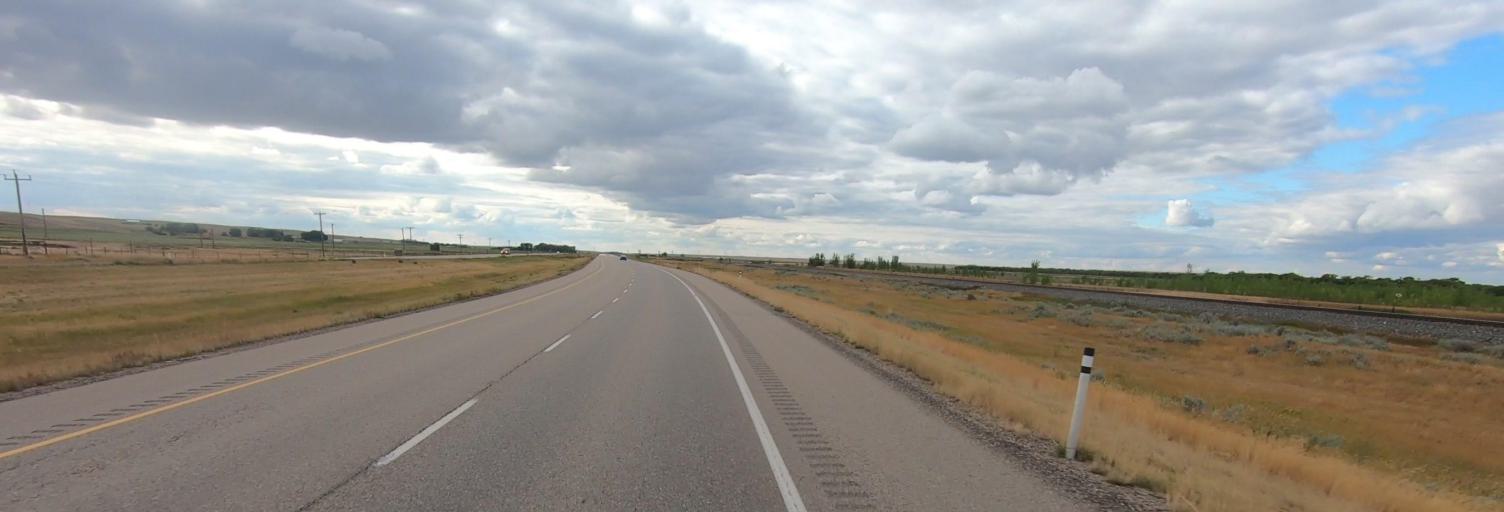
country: CA
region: Alberta
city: Medicine Hat
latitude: 49.9752
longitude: -110.3863
